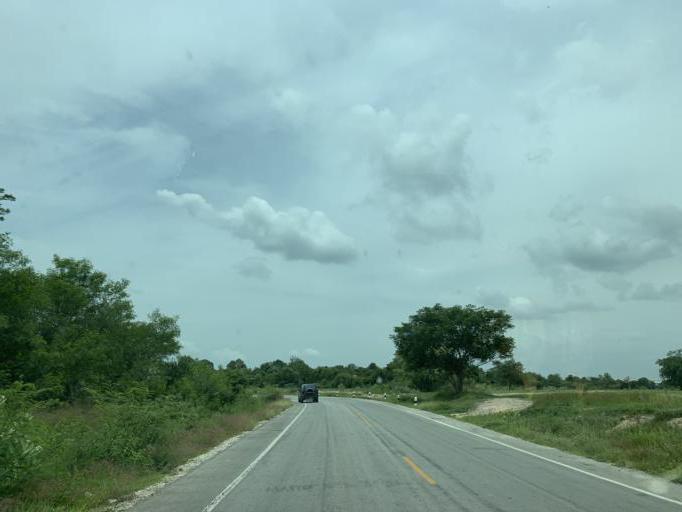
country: TH
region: Uthai Thani
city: Uthai Thani
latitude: 15.4042
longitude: 100.0260
